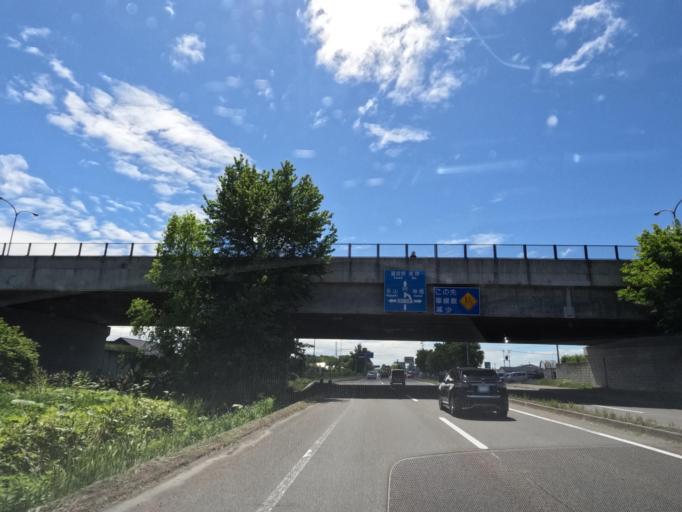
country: JP
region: Hokkaido
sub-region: Asahikawa-shi
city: Asahikawa
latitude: 43.7269
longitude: 142.3678
